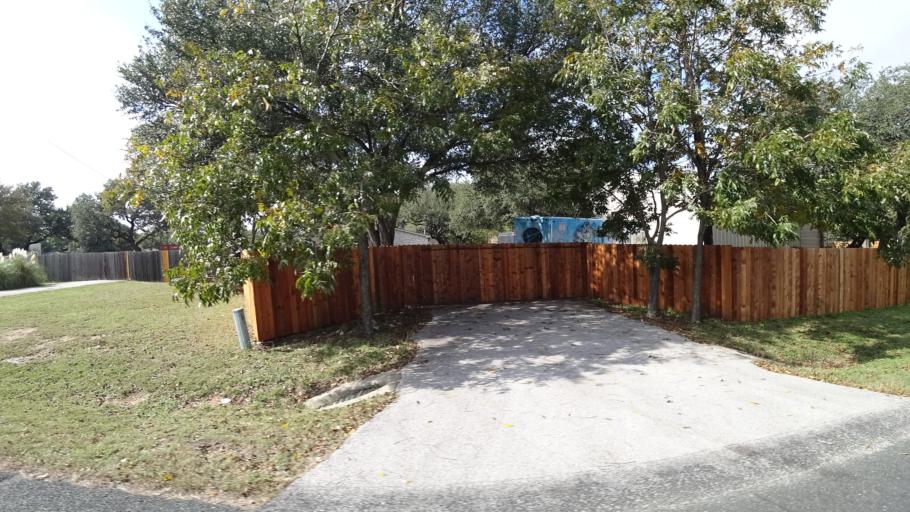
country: US
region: Texas
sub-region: Williamson County
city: Brushy Creek
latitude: 30.5293
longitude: -97.7374
